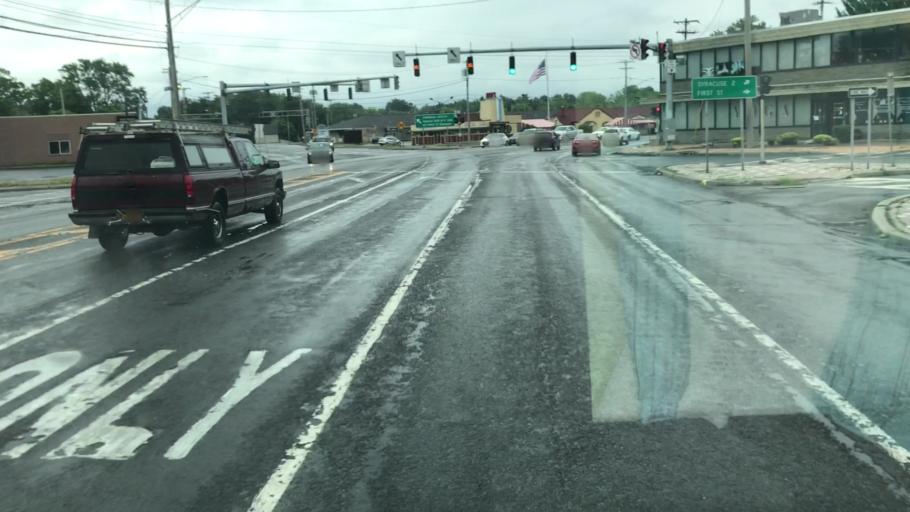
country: US
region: New York
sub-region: Onondaga County
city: Liverpool
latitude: 43.1018
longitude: -76.2034
